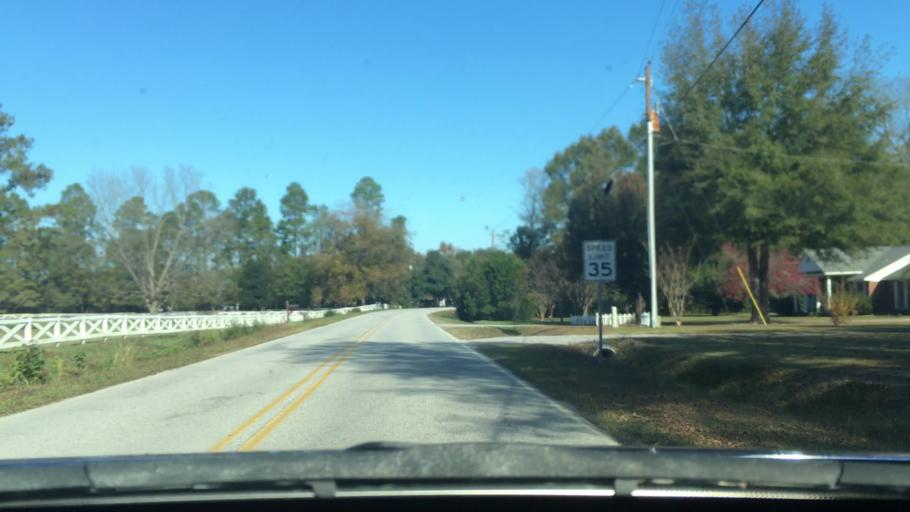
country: US
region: South Carolina
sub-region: Sumter County
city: Cane Savannah
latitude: 33.9113
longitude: -80.4122
